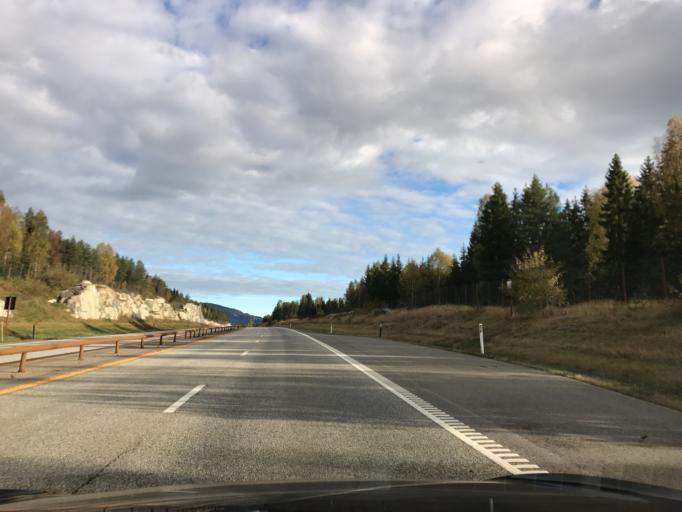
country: NO
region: Akershus
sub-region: Eidsvoll
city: Raholt
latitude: 60.2951
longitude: 11.1369
